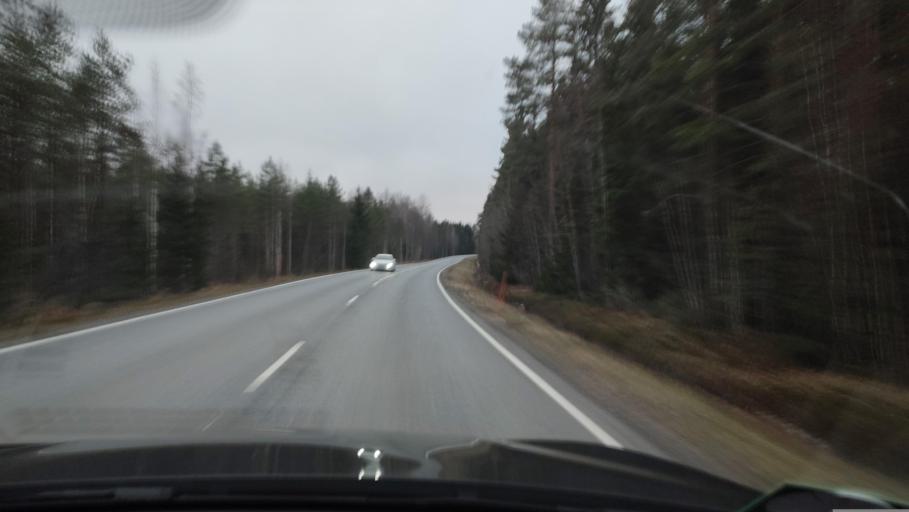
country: FI
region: Southern Ostrobothnia
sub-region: Suupohja
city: Karijoki
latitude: 62.3233
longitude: 21.8784
